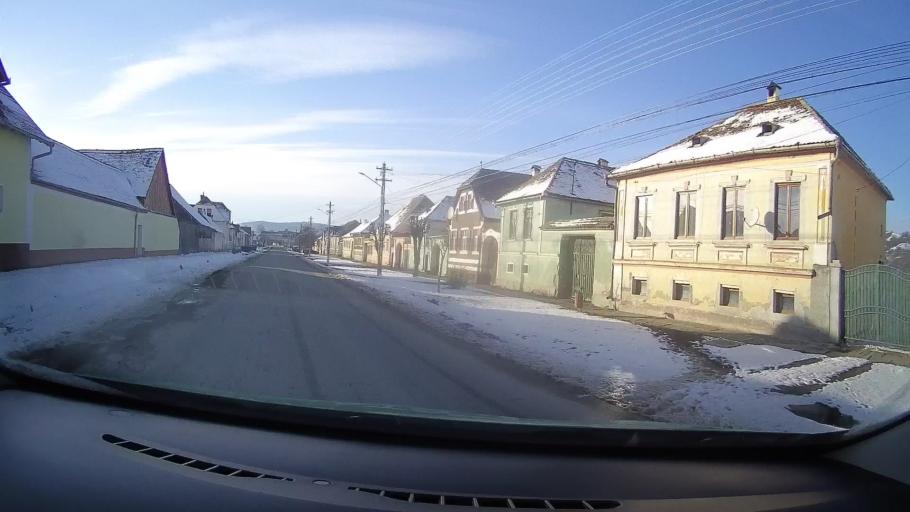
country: RO
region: Sibiu
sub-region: Comuna Merghindeal
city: Merghindeal
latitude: 45.9660
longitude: 24.7243
